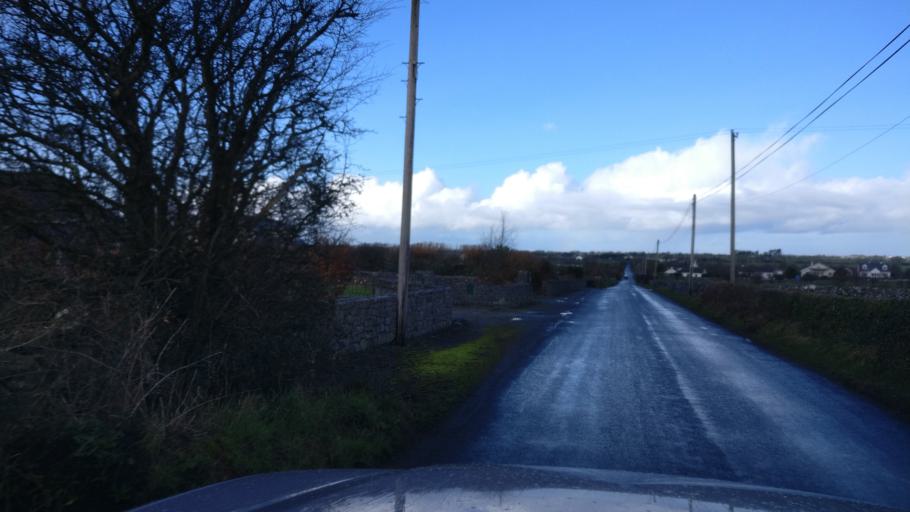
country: IE
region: Connaught
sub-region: County Galway
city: Oranmore
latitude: 53.2633
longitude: -8.8667
